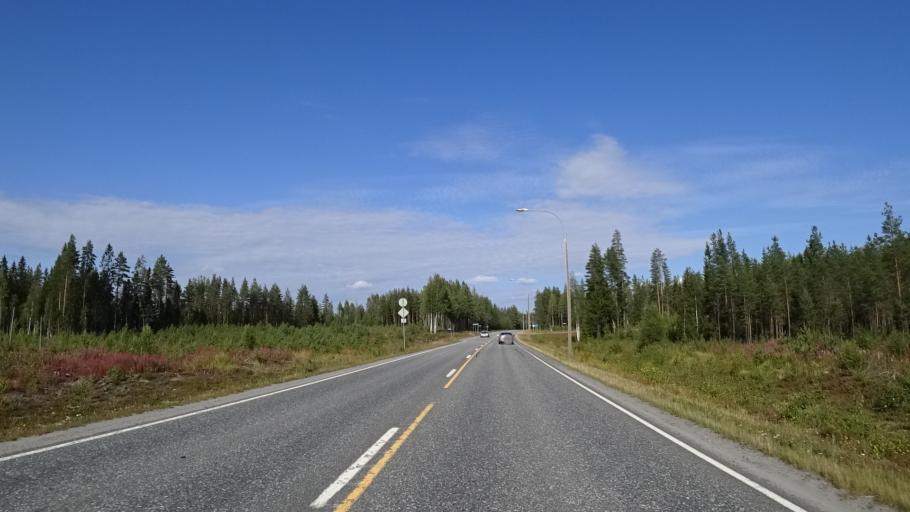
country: FI
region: North Karelia
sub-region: Joensuu
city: Eno
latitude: 62.7705
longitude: 30.0476
